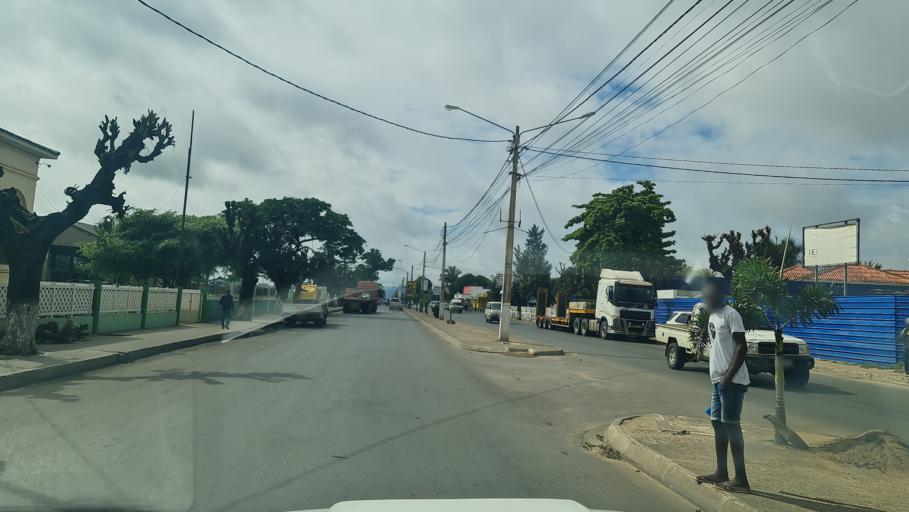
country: MZ
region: Nampula
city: Nampula
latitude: -15.1137
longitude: 39.2635
